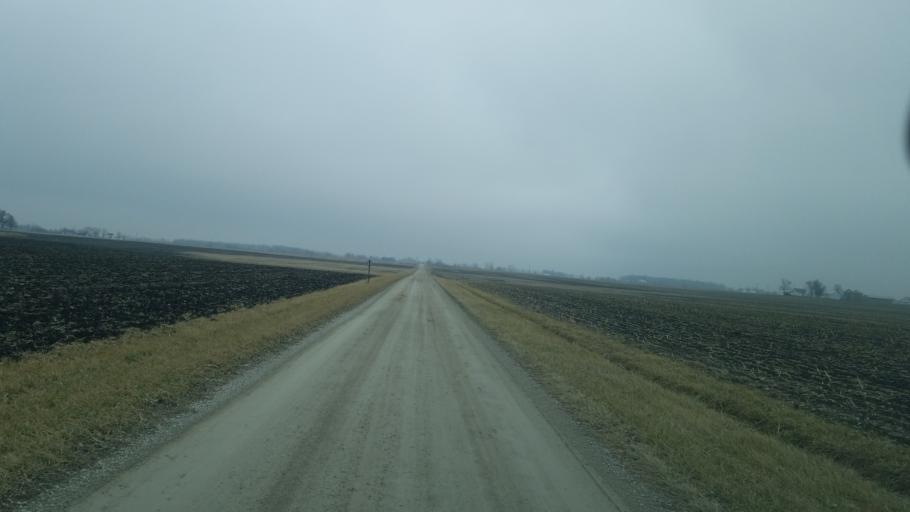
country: US
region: Indiana
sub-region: Adams County
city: Berne
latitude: 40.6738
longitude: -84.8580
